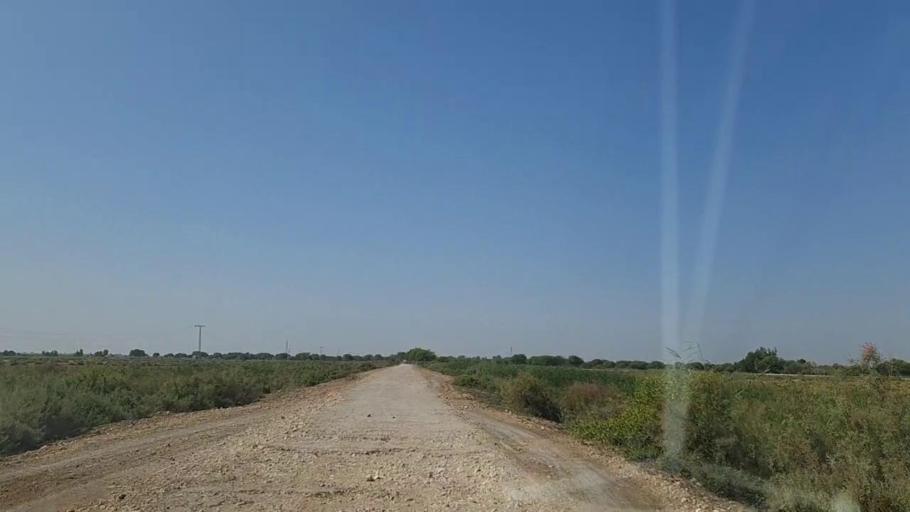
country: PK
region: Sindh
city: Chuhar Jamali
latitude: 24.4161
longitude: 68.0336
